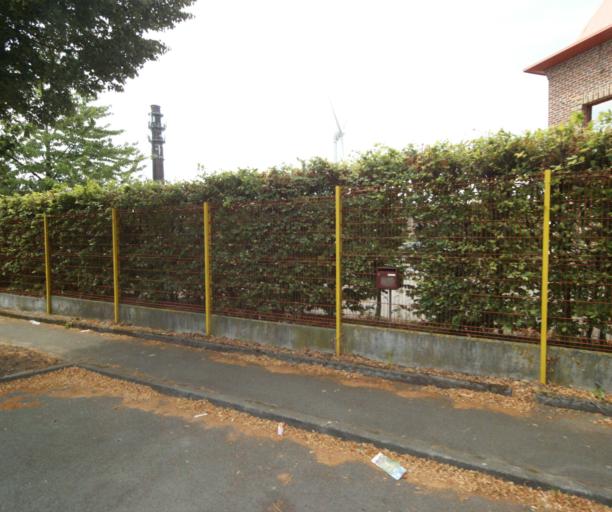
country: FR
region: Nord-Pas-de-Calais
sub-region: Departement du Nord
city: Mouvaux
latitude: 50.7189
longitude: 3.1332
